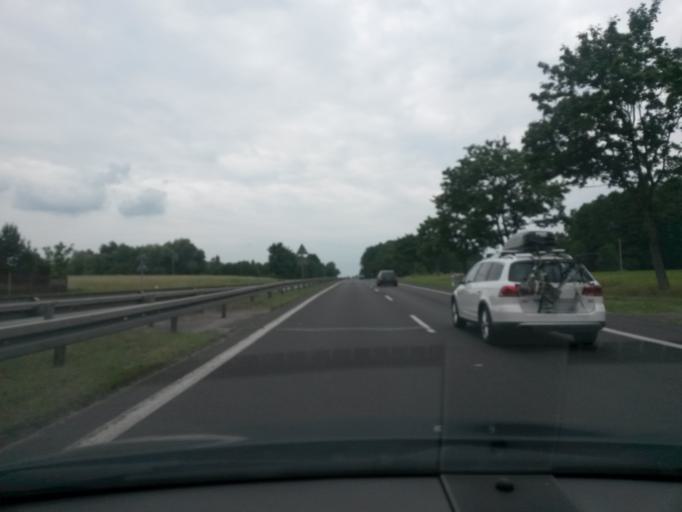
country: PL
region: Lodz Voivodeship
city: Zabia Wola
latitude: 52.0172
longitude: 20.6272
